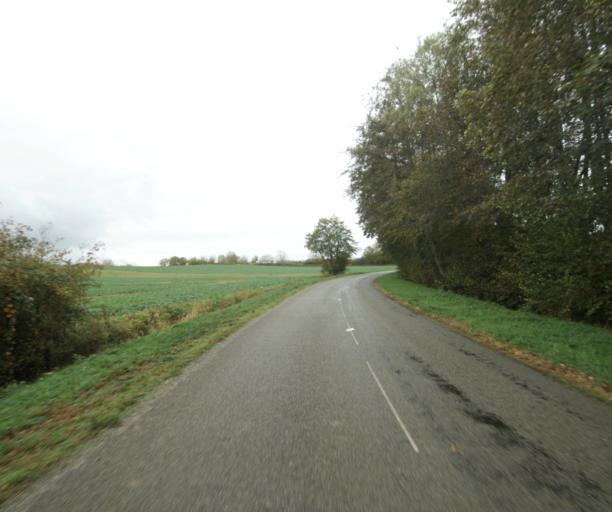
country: FR
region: Rhone-Alpes
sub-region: Departement de l'Ain
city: Pont-de-Vaux
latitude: 46.4753
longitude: 4.8903
